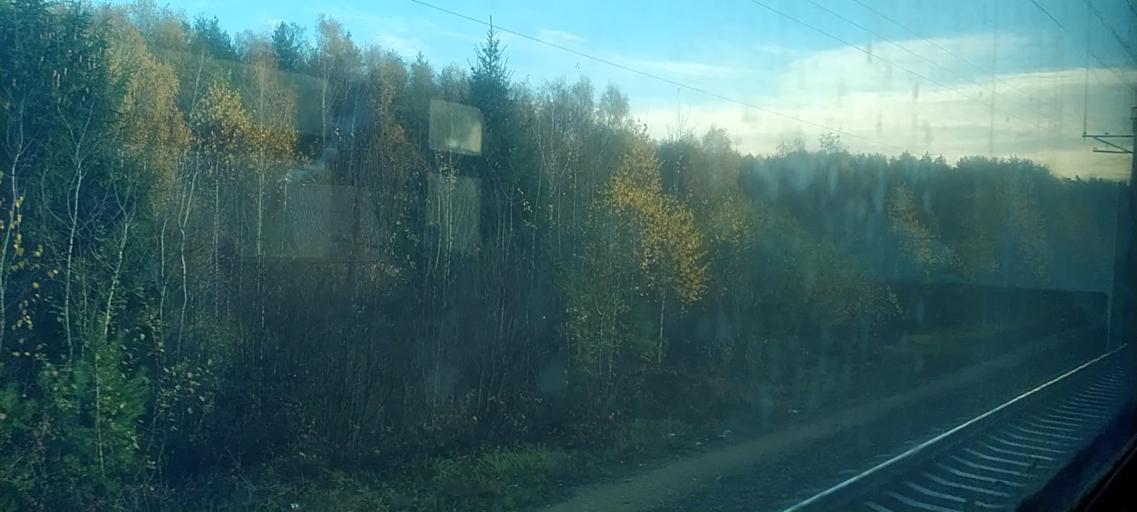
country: RU
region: Moskovskaya
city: Il'inskiy
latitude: 55.6472
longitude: 38.1182
